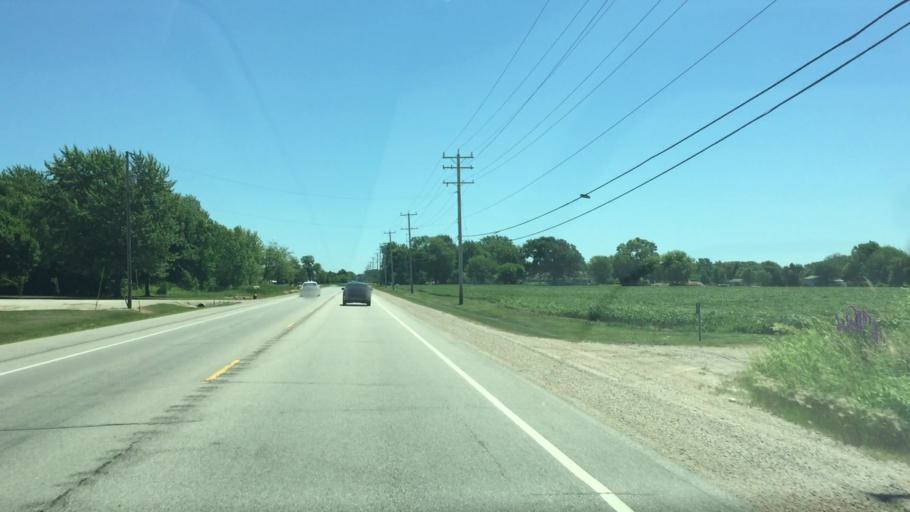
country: US
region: Wisconsin
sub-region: Calumet County
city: Sherwood
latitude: 44.1971
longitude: -88.3086
